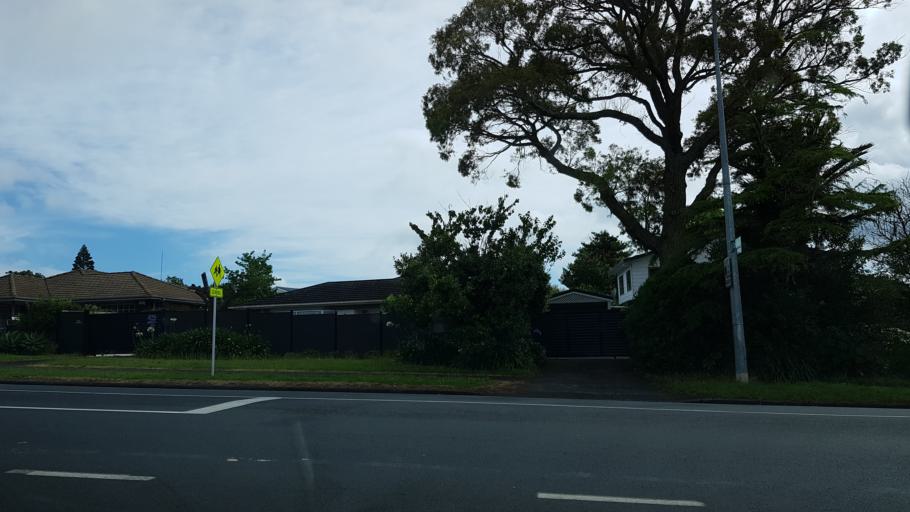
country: NZ
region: Auckland
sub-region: Auckland
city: North Shore
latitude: -36.7905
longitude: 174.7459
